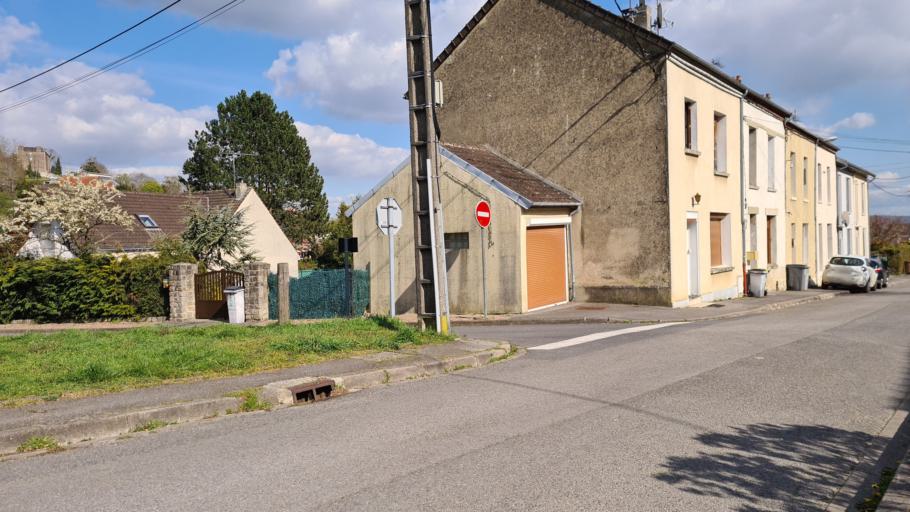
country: FR
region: Picardie
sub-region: Departement de l'Aisne
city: Laon
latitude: 49.5595
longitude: 3.6215
